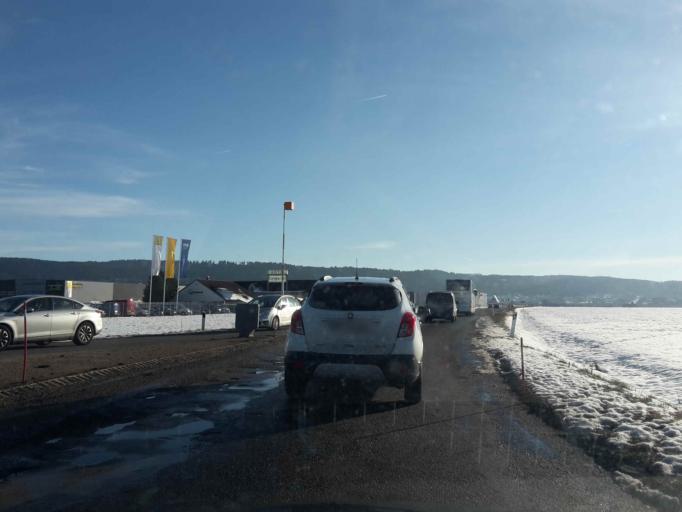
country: FR
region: Franche-Comte
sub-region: Departement du Doubs
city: Pontarlier
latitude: 46.9100
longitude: 6.3321
